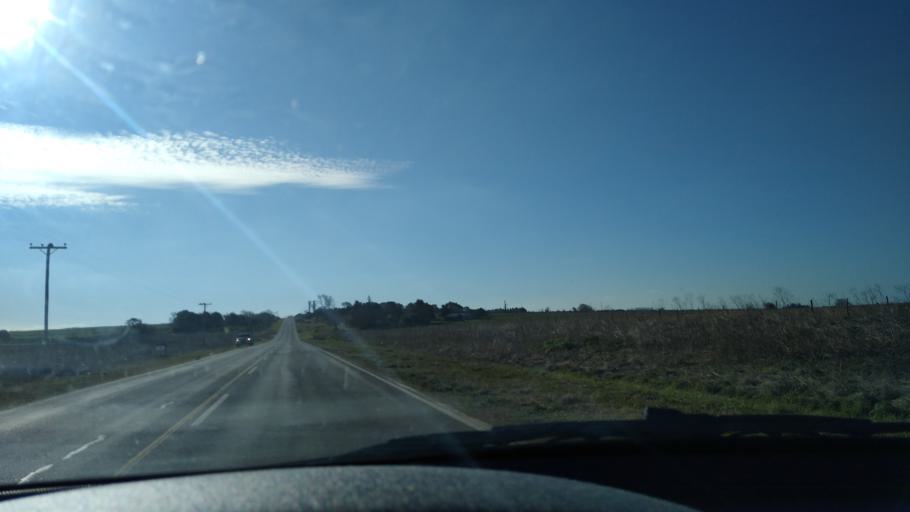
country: AR
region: Entre Rios
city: Aranguren
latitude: -32.3712
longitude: -60.3420
